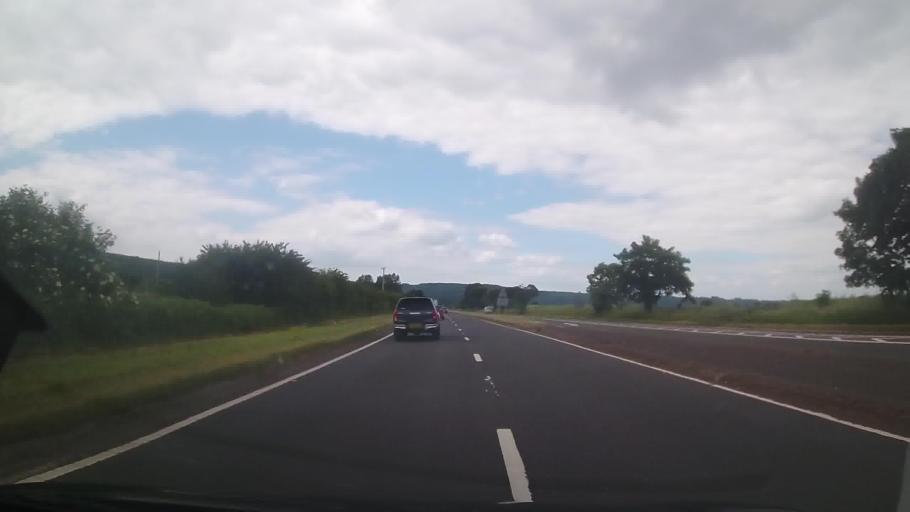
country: GB
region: England
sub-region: Herefordshire
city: Wellington
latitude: 52.1297
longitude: -2.7311
